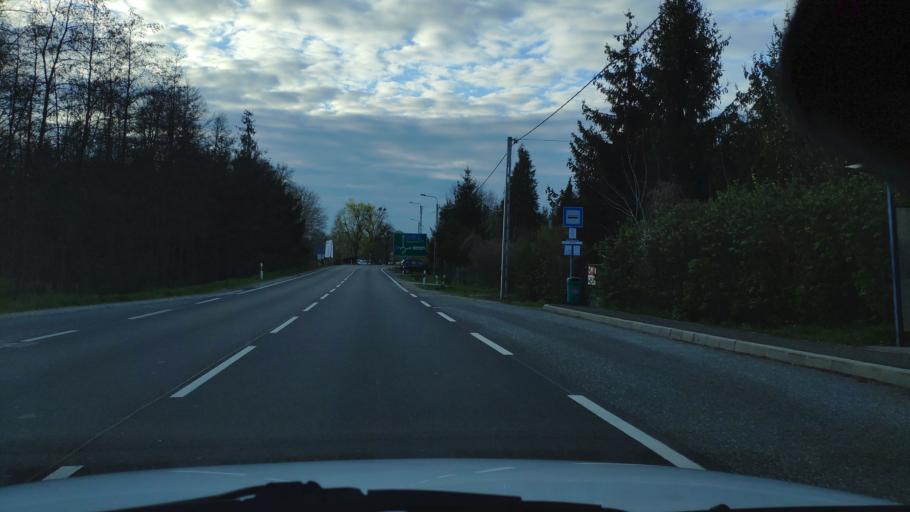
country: HU
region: Zala
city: Nagykanizsa
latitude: 46.4399
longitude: 17.0354
